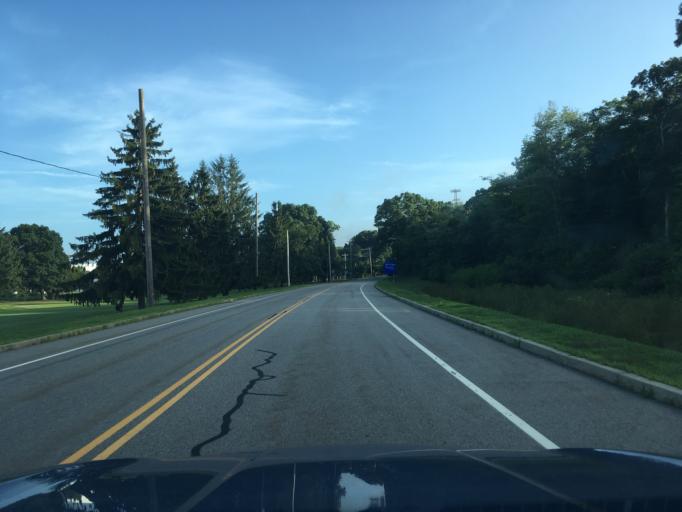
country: US
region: Rhode Island
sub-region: Washington County
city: North Kingstown
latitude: 41.6016
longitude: -71.4261
